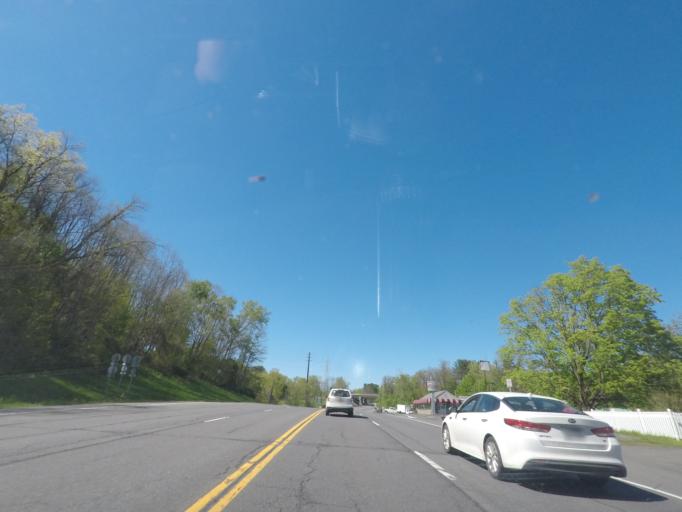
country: US
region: New York
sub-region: Greene County
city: Catskill
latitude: 42.2287
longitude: -73.8699
